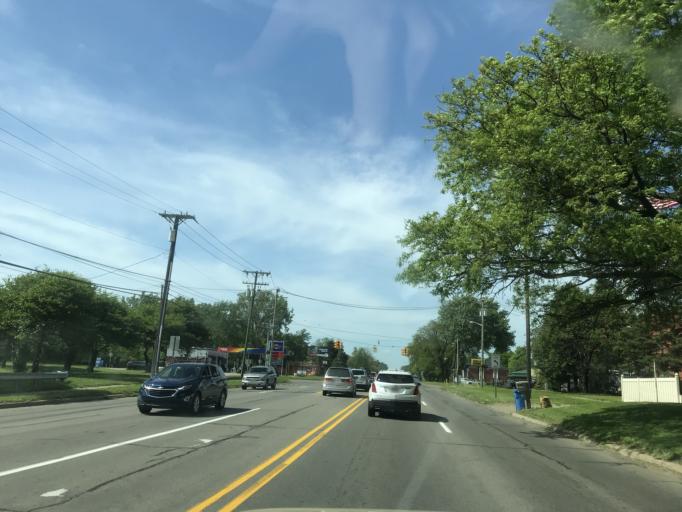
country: US
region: Michigan
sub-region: Wayne County
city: Garden City
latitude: 42.3501
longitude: -83.3125
